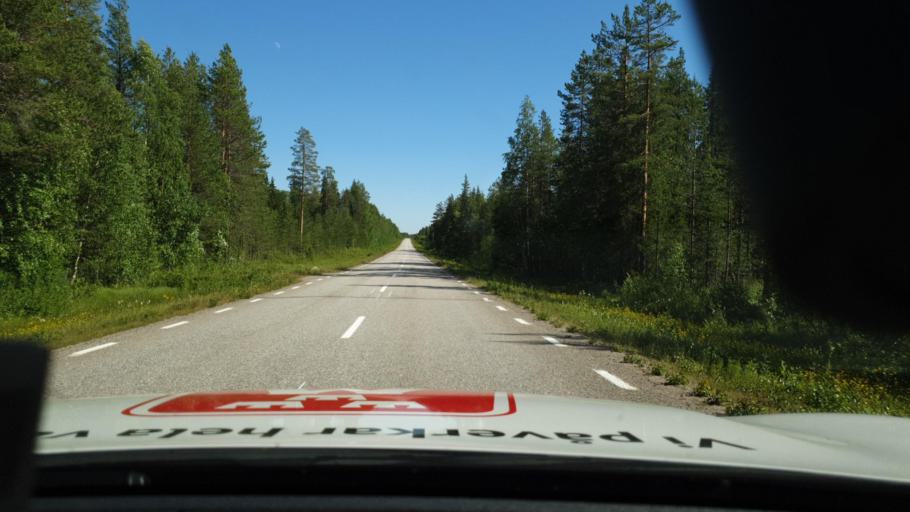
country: SE
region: Norrbotten
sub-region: Lulea Kommun
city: Ranea
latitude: 65.9868
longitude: 22.3499
